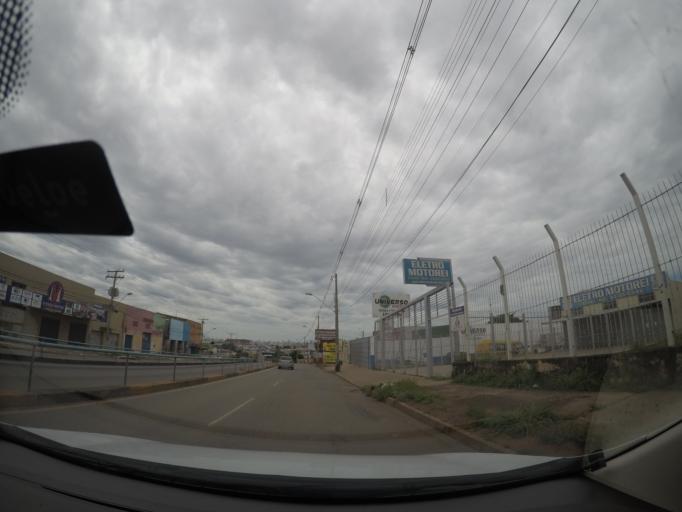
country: BR
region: Goias
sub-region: Goiania
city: Goiania
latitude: -16.6640
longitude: -49.3212
